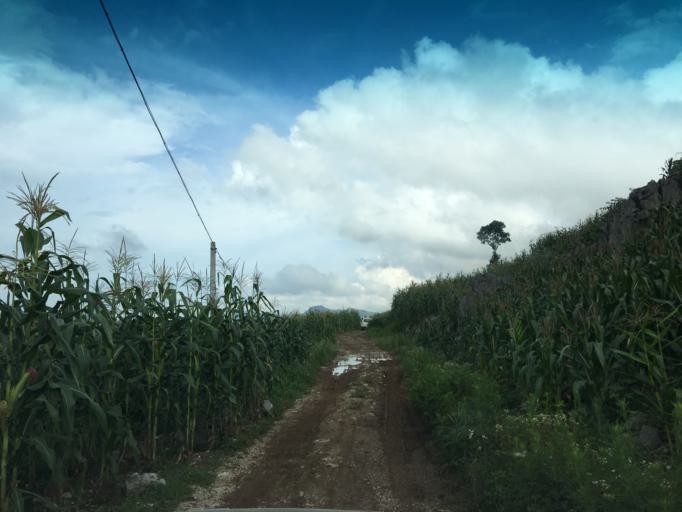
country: CN
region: Guangxi Zhuangzu Zizhiqu
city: Xinzhou
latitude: 24.9922
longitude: 105.6342
